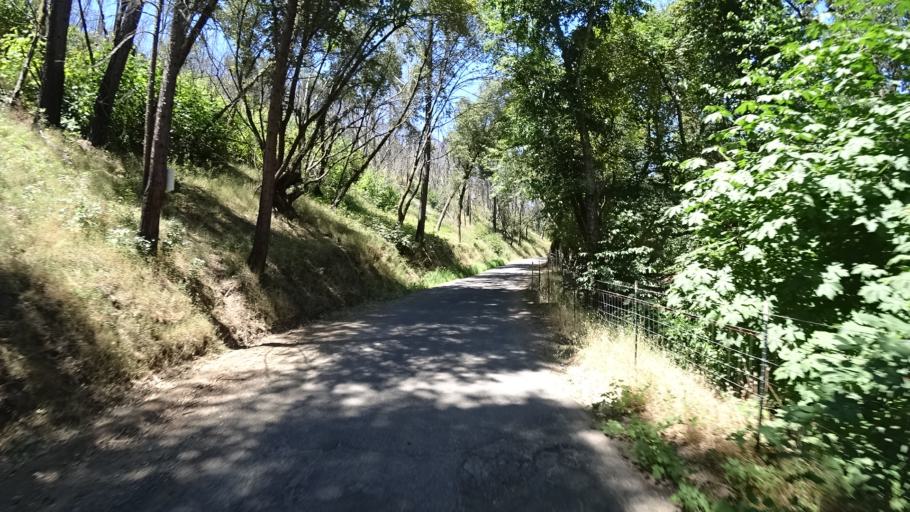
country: US
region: California
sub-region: Calaveras County
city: Mountain Ranch
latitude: 38.1936
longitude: -120.5803
